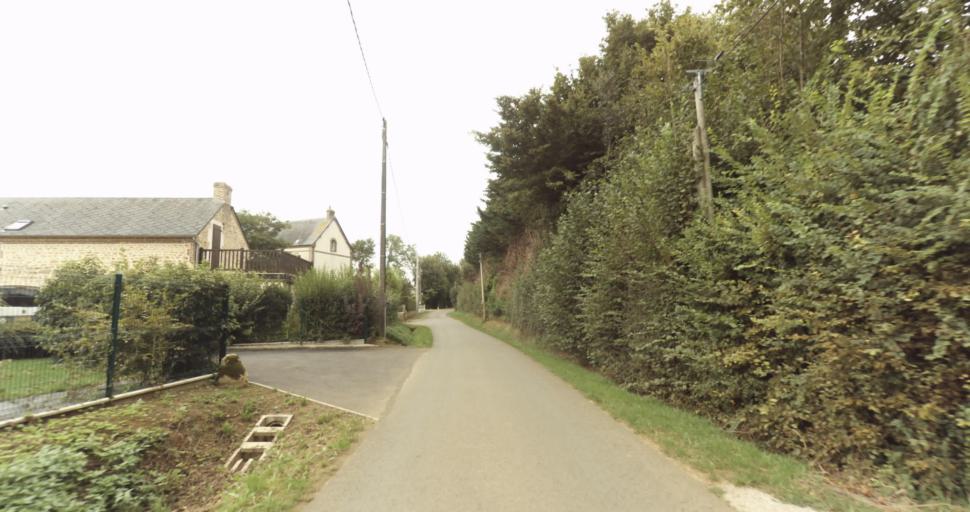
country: FR
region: Lower Normandy
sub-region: Departement de l'Orne
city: Gace
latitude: 48.7278
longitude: 0.3257
